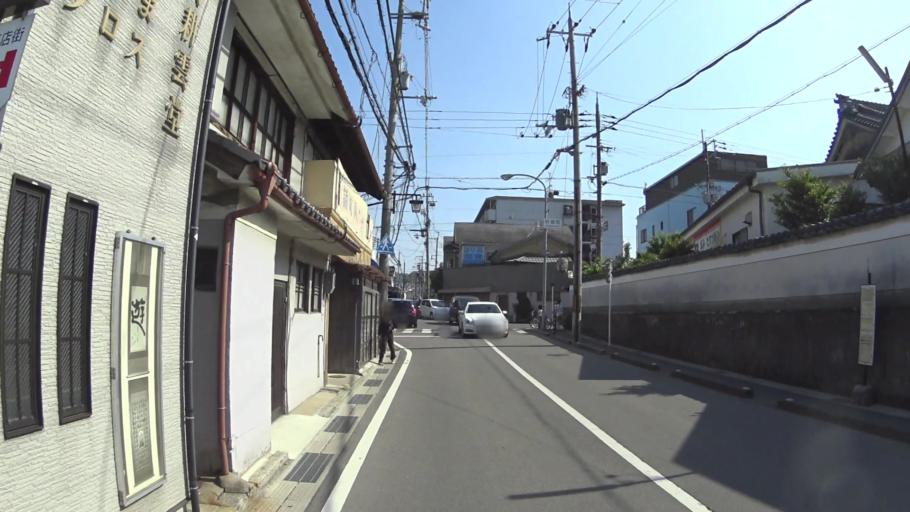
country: JP
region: Kyoto
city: Kameoka
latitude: 35.0102
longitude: 135.5834
